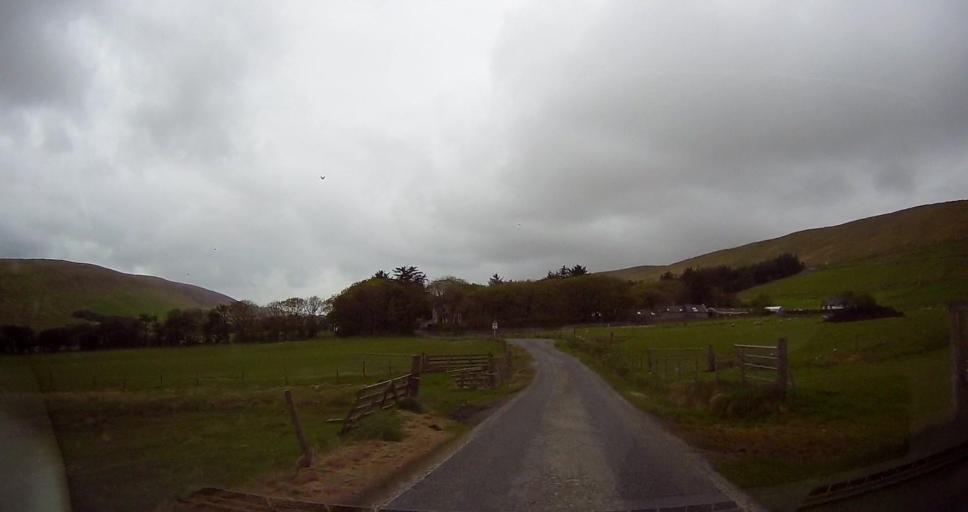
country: GB
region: Scotland
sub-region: Shetland Islands
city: Lerwick
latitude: 60.2727
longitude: -1.2857
